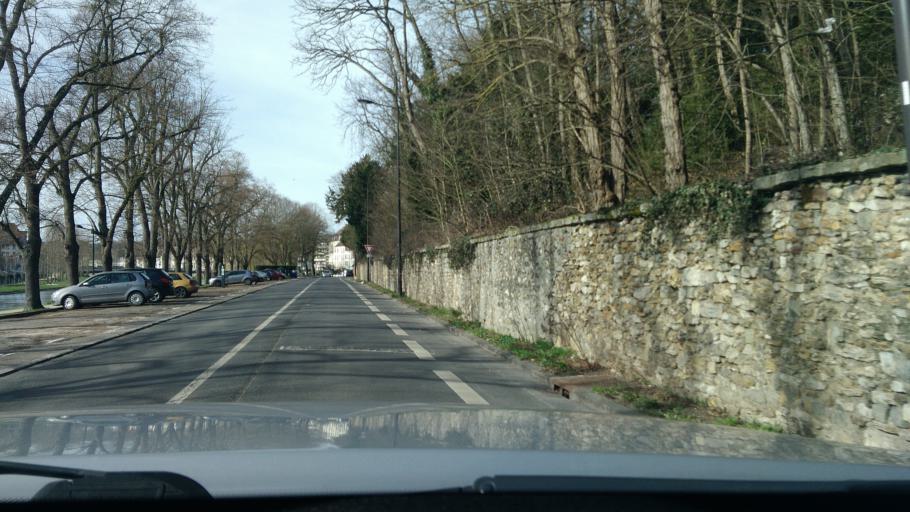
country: FR
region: Ile-de-France
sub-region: Departement de Seine-et-Marne
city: Melun
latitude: 48.5348
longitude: 2.6649
